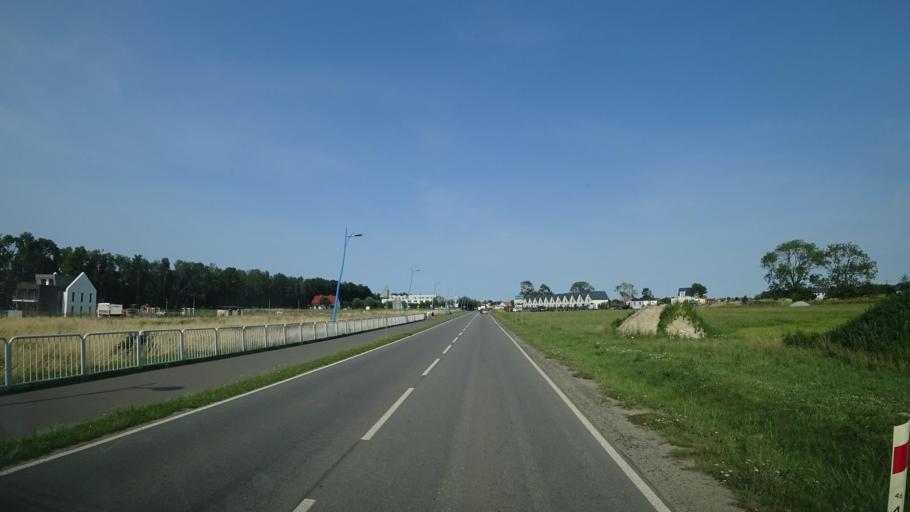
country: PL
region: West Pomeranian Voivodeship
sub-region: Powiat gryficki
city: Rewal
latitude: 54.0782
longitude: 14.9978
